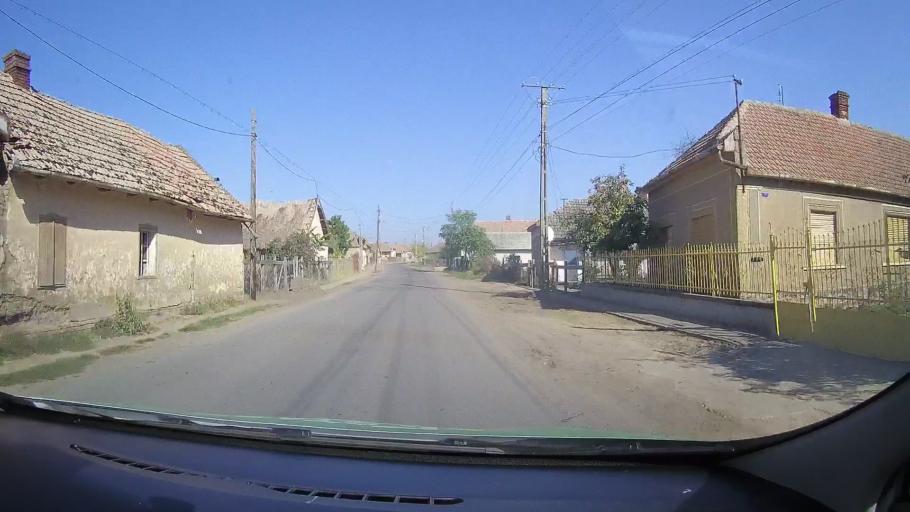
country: RO
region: Satu Mare
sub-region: Comuna Ciumesti
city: Ciumesti
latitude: 47.6561
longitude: 22.3337
